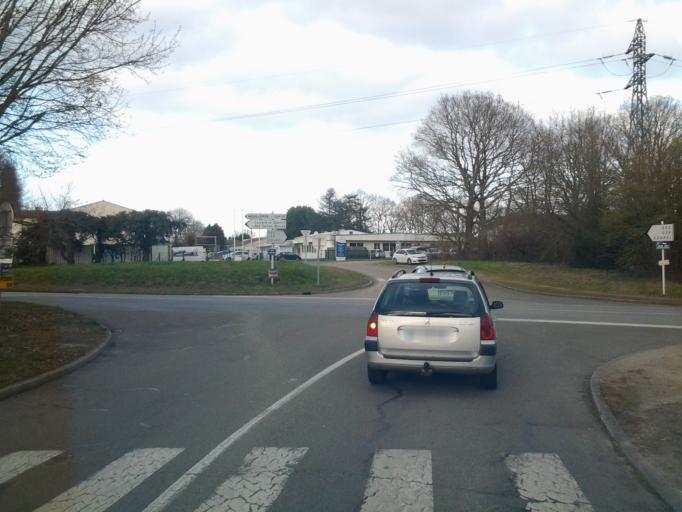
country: FR
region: Pays de la Loire
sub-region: Departement de la Vendee
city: La Roche-sur-Yon
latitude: 46.6910
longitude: -1.4401
